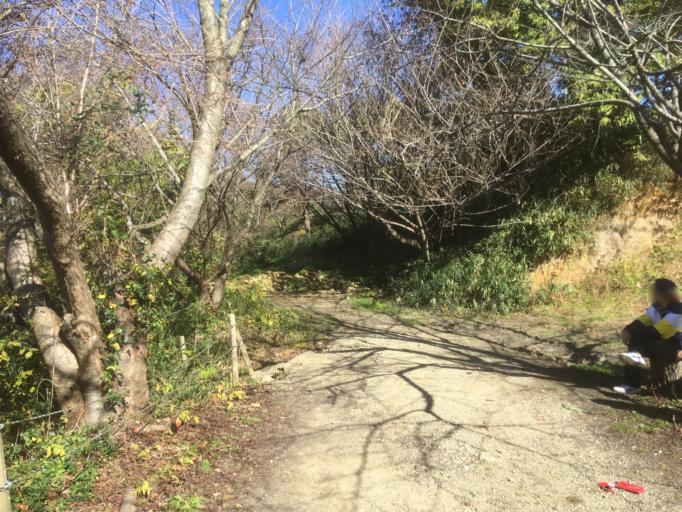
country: JP
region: Osaka
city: Kashihara
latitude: 34.6052
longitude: 135.6596
